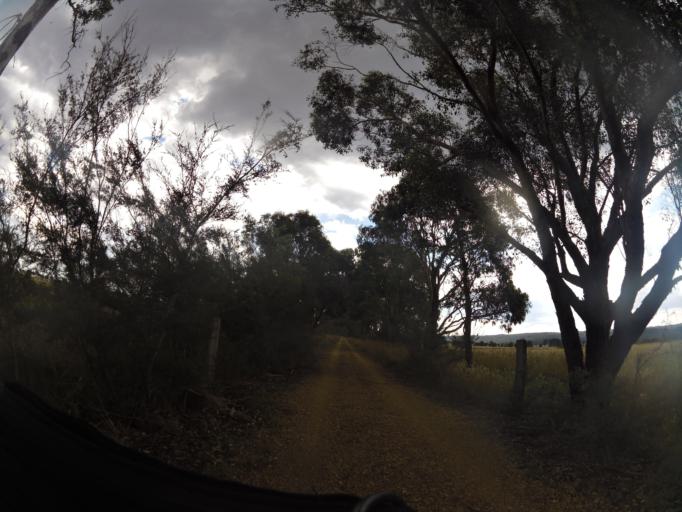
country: AU
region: Victoria
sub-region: Wellington
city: Heyfield
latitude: -38.0183
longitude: 146.6847
